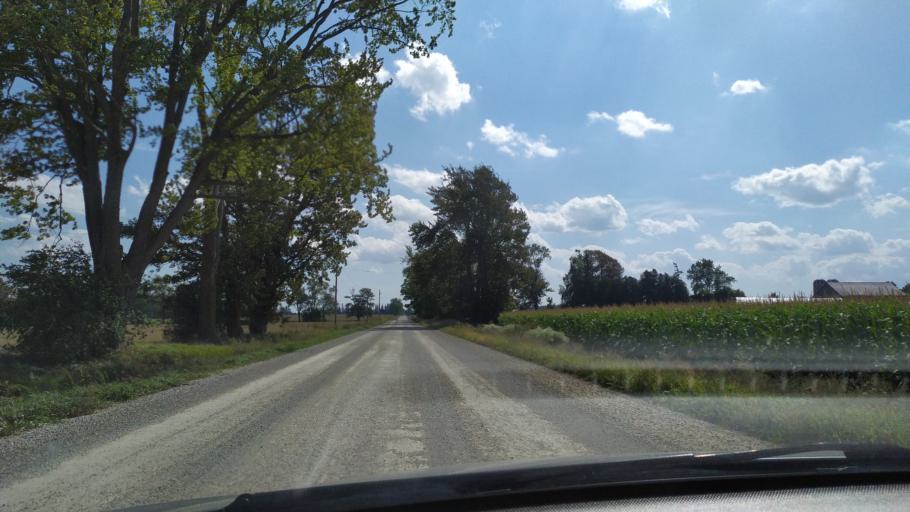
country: CA
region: Ontario
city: Stratford
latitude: 43.2829
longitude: -80.9278
